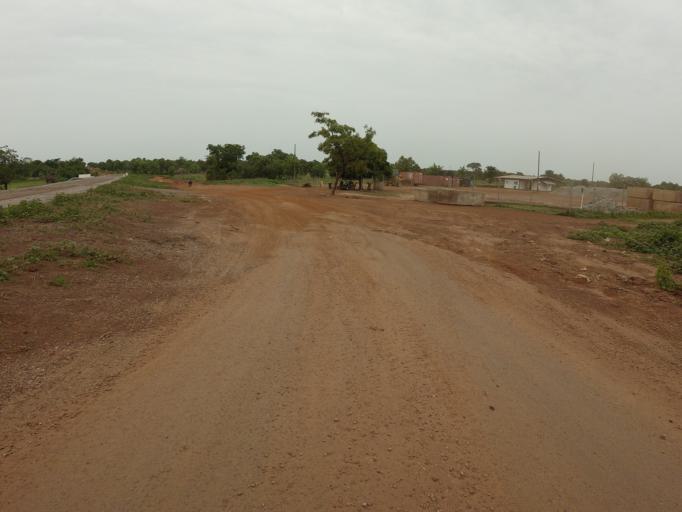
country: GH
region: Northern
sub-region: Yendi
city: Yendi
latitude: 9.0662
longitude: -0.0114
